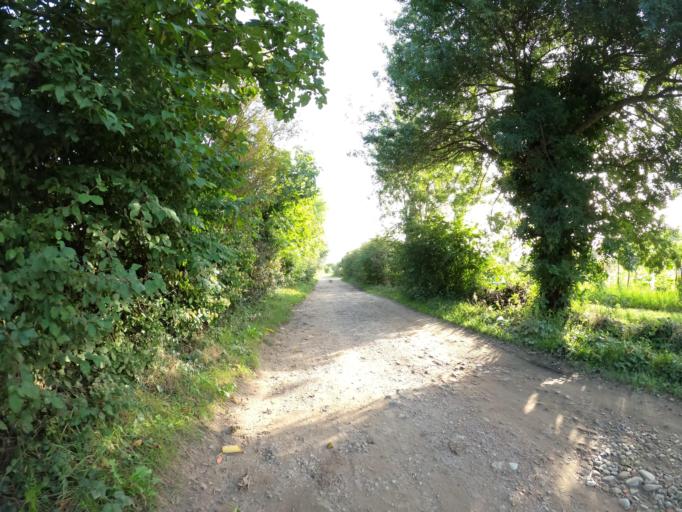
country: FR
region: Midi-Pyrenees
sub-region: Departement de la Haute-Garonne
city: Portet-sur-Garonne
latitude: 43.5396
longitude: 1.4230
